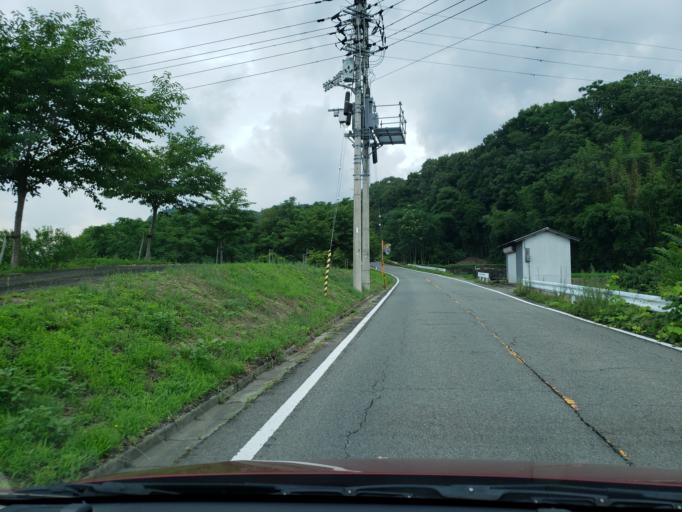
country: JP
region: Tokushima
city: Kamojimacho-jogejima
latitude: 34.1031
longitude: 134.2775
